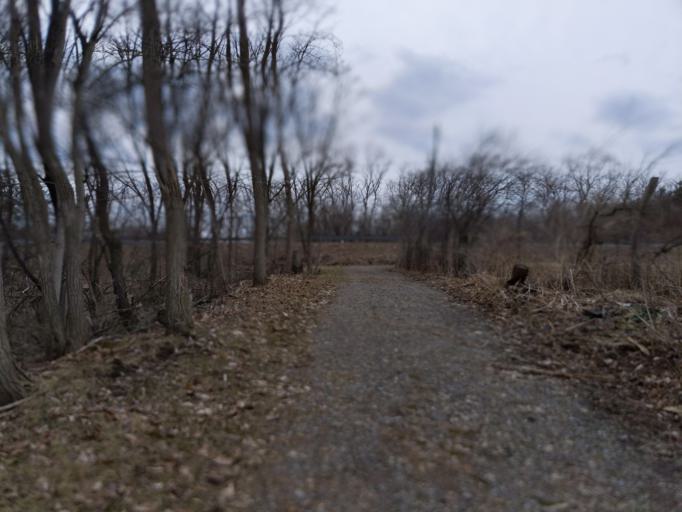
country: US
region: New York
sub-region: Tompkins County
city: Dryden
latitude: 42.4977
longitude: -76.3280
